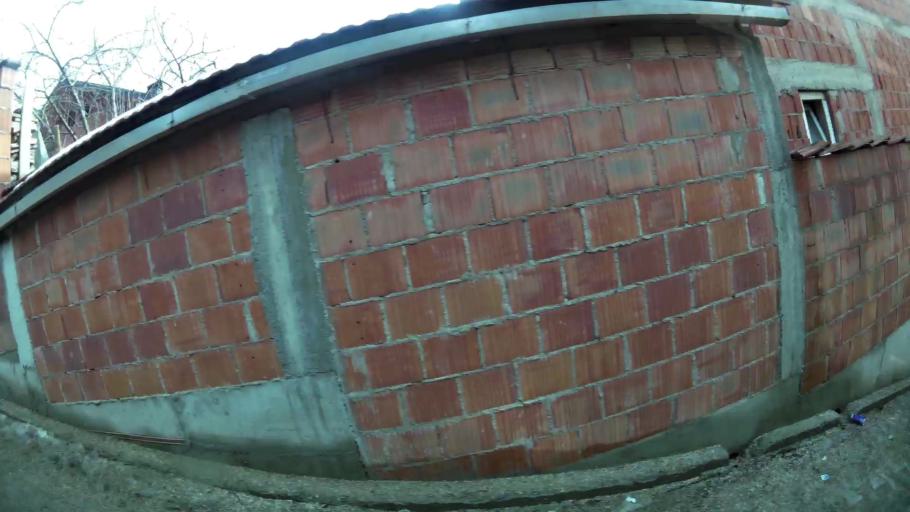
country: XK
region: Pristina
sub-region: Komuna e Prishtines
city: Pristina
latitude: 42.6843
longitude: 21.1699
